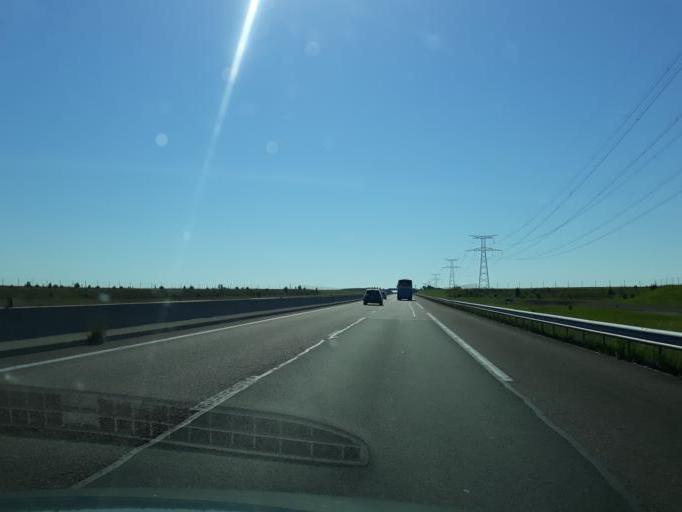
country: FR
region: Centre
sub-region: Departement du Loiret
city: Boynes
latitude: 48.1011
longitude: 2.3394
